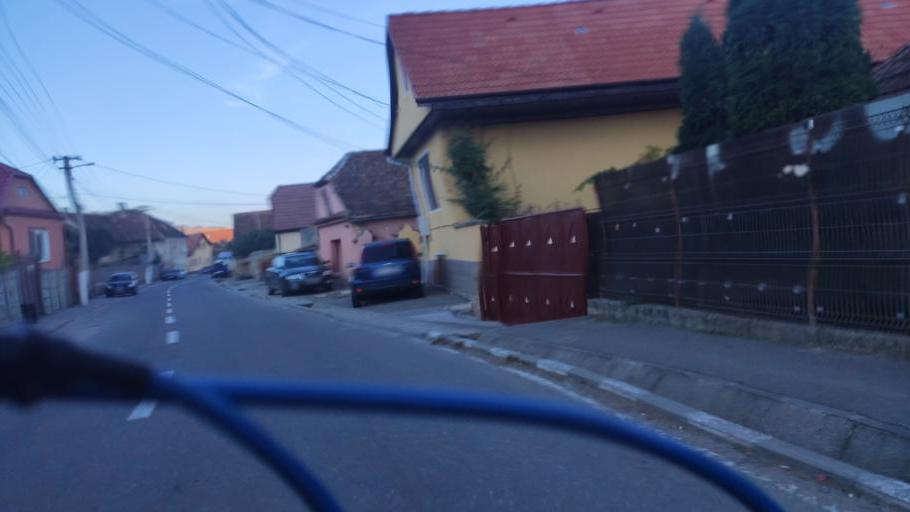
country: RO
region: Brasov
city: Codlea
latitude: 45.6945
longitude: 25.4426
